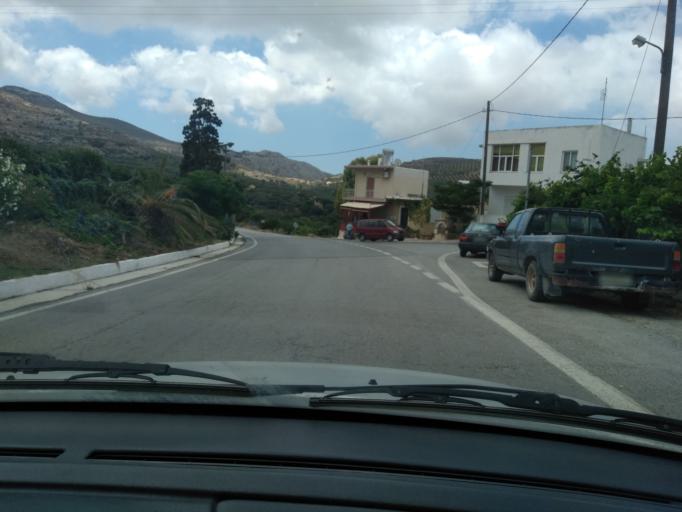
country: GR
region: Crete
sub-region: Nomos Lasithiou
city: Makry-Gialos
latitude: 35.0738
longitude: 26.0469
